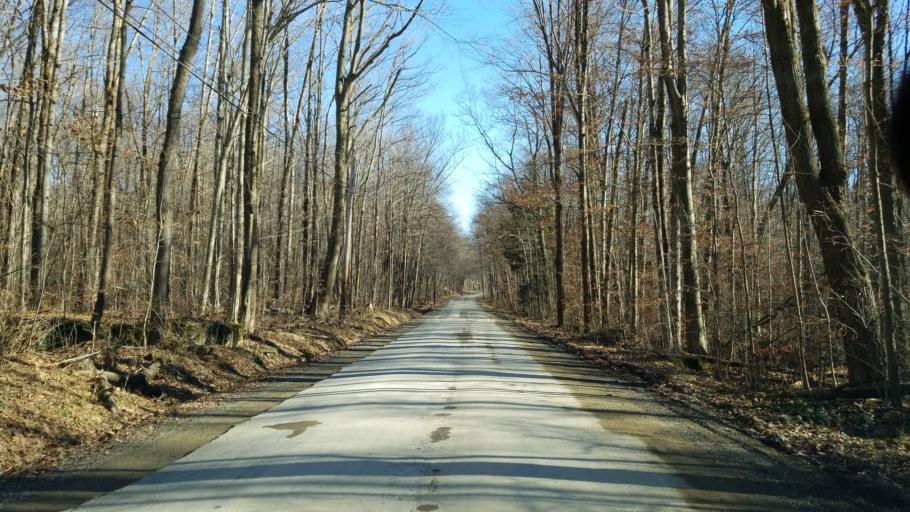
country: US
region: Pennsylvania
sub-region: Jefferson County
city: Falls Creek
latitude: 41.1596
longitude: -78.8370
